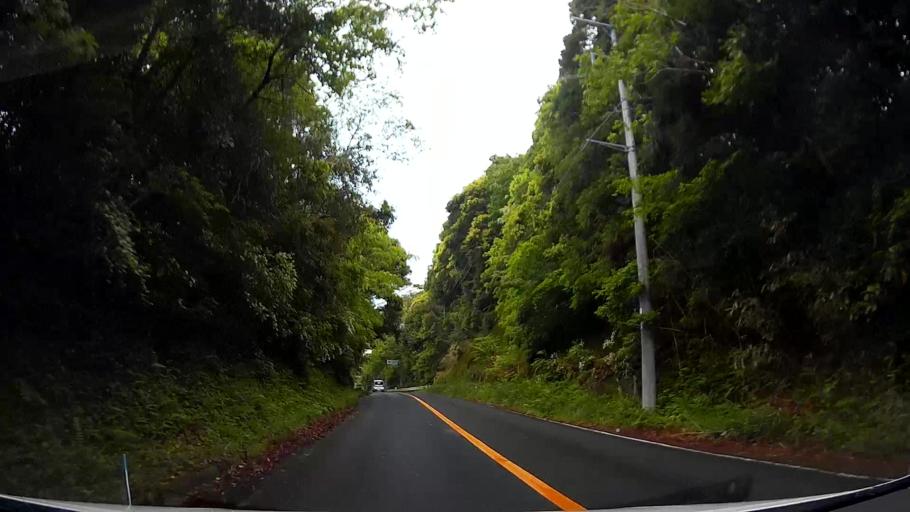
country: JP
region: Shizuoka
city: Shimoda
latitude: 34.7060
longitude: 138.7589
